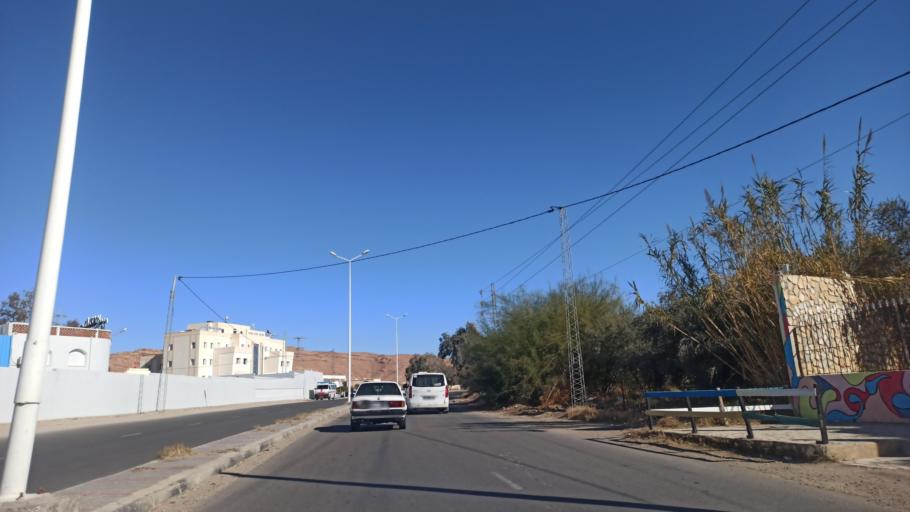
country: TN
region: Gafsa
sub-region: Gafsa Municipality
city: Gafsa
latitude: 34.4208
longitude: 8.7460
